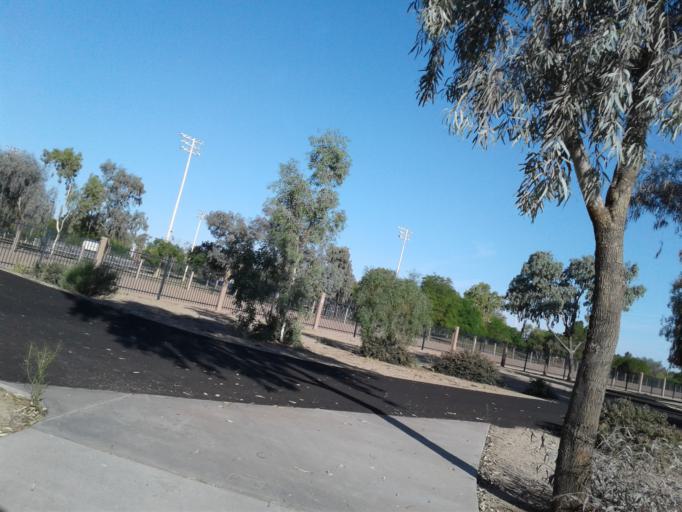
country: US
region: Arizona
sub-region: Maricopa County
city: Glendale
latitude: 33.5780
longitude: -112.1099
